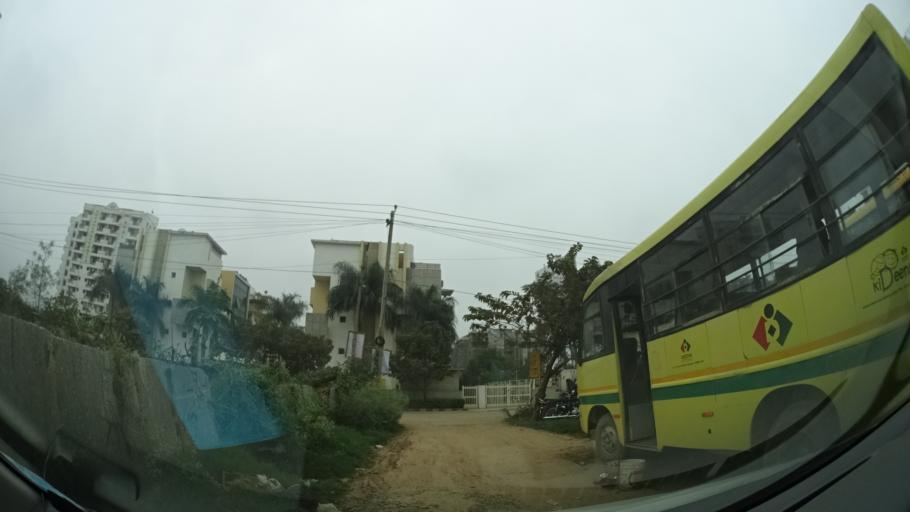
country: IN
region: Karnataka
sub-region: Bangalore Rural
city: Hoskote
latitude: 12.9757
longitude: 77.7437
